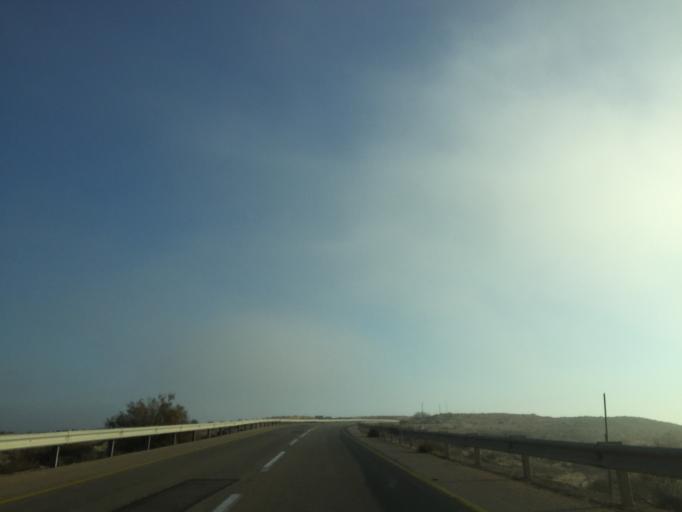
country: IL
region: Southern District
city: Yeroham
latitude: 30.9958
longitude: 34.9243
